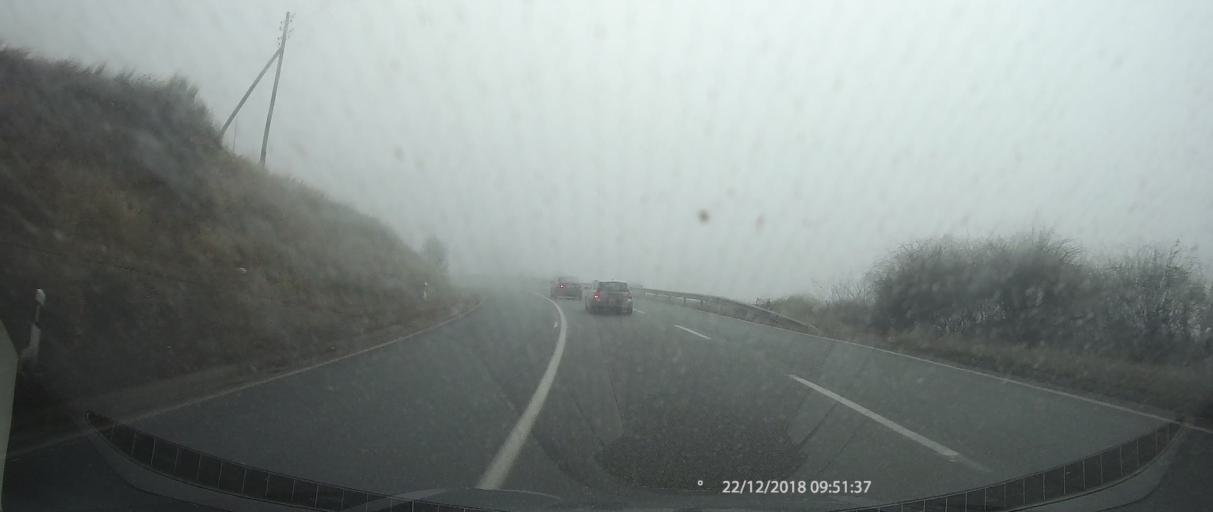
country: MK
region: Staro Nagoricane
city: Staro Nagorichane
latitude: 42.1691
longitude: 21.8082
